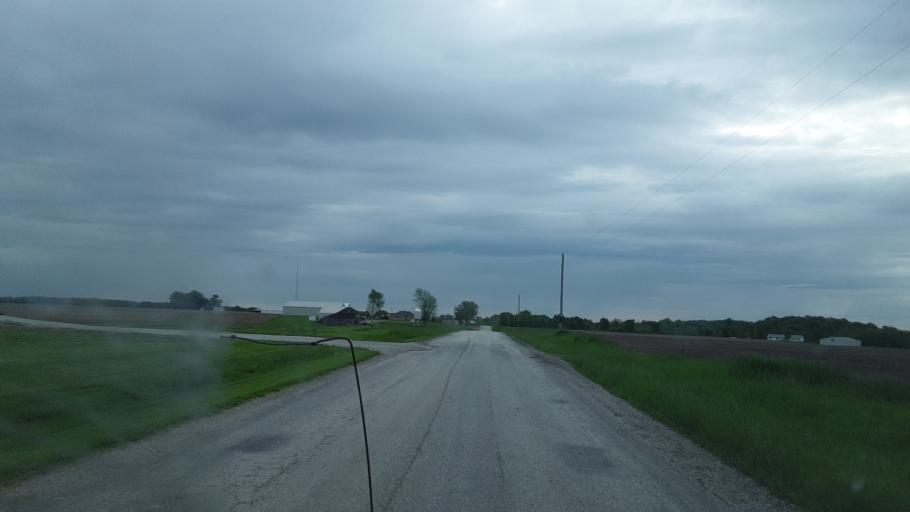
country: US
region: Illinois
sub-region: McDonough County
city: Macomb
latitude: 40.3816
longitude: -90.6173
